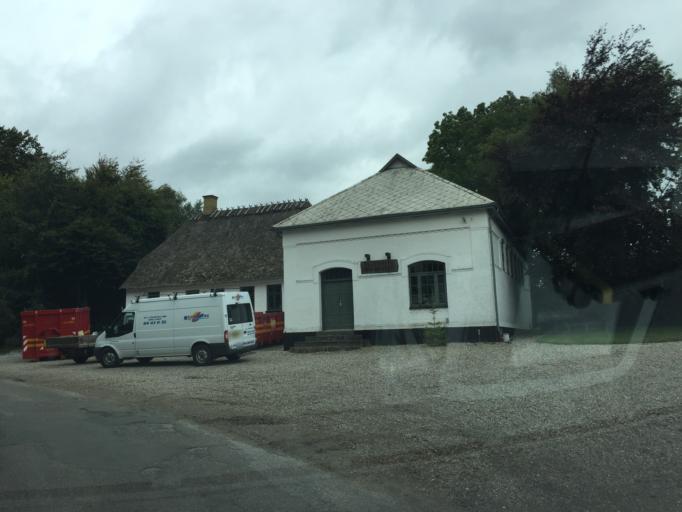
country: DK
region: South Denmark
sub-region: Assens Kommune
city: Arup
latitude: 55.3641
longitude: 10.0471
